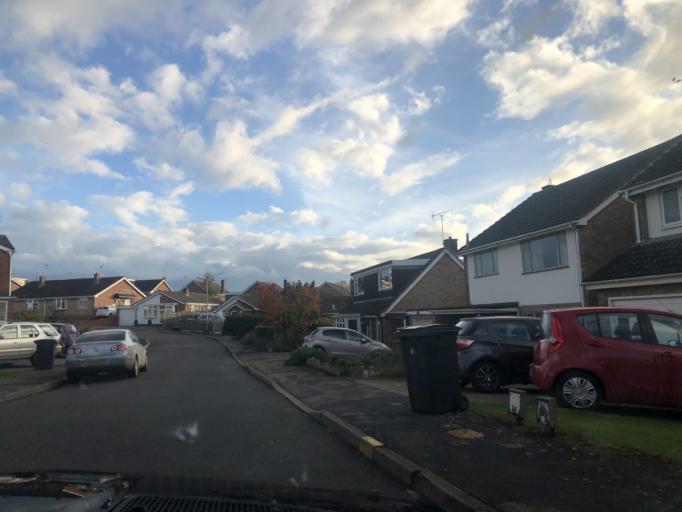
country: GB
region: England
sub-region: Warwickshire
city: Harbury
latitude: 52.2357
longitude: -1.4654
